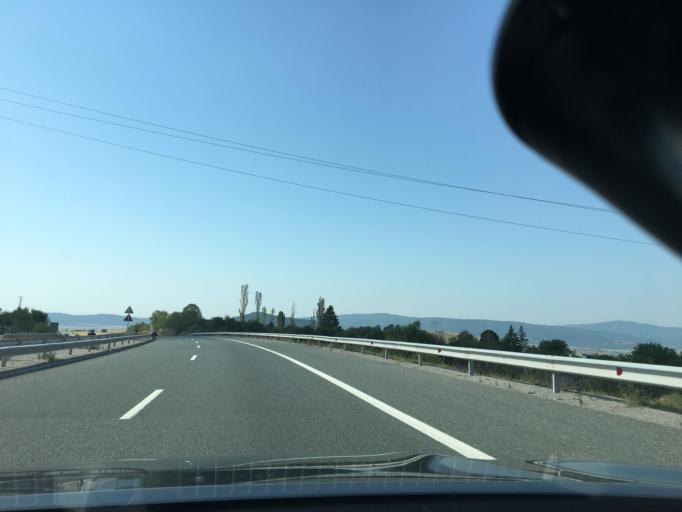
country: BG
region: Pernik
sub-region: Obshtina Pernik
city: Pernik
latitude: 42.4788
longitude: 23.1121
